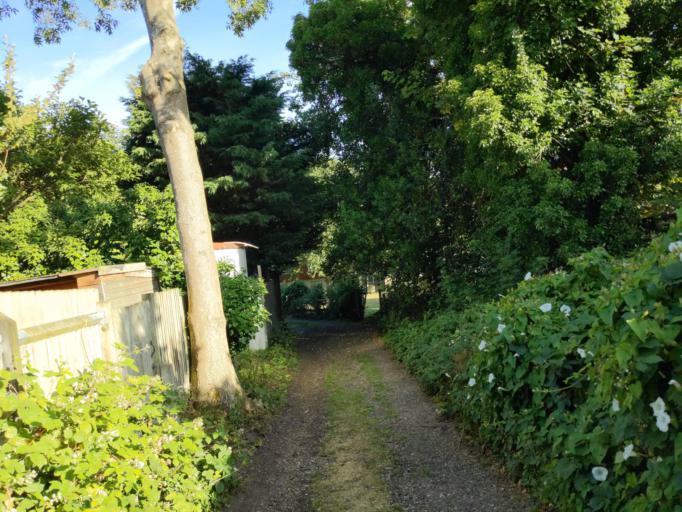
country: GB
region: England
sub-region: Greater London
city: West Wickham
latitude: 51.3752
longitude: 0.0095
